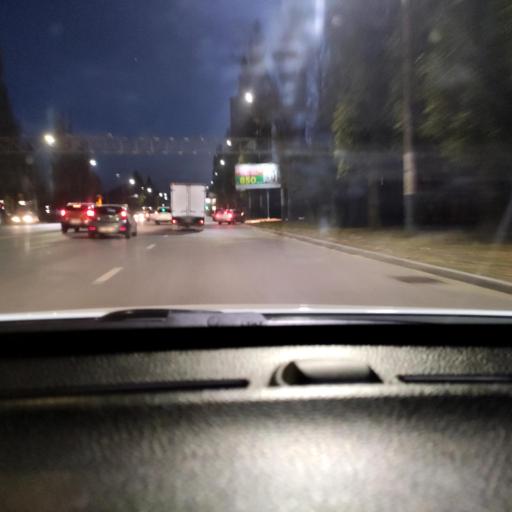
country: RU
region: Voronezj
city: Somovo
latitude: 51.7061
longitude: 39.2761
